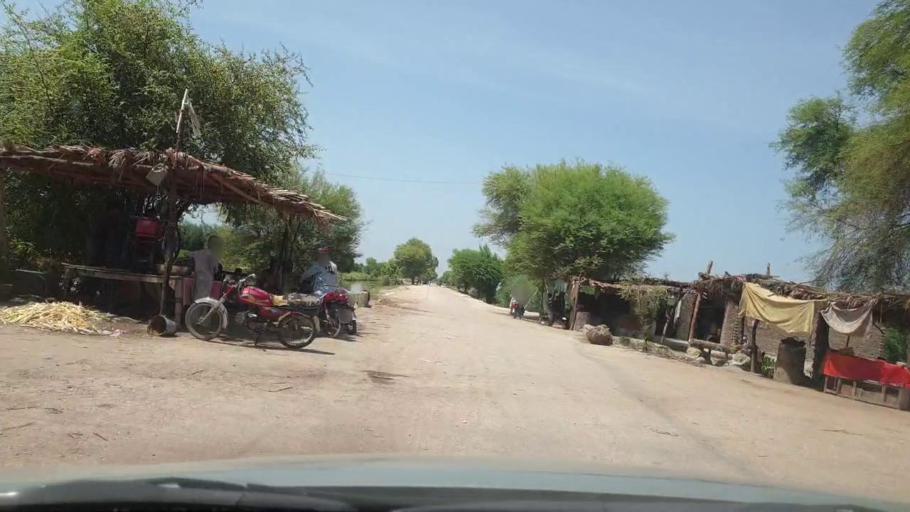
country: PK
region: Sindh
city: Pano Aqil
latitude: 27.7064
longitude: 69.1130
